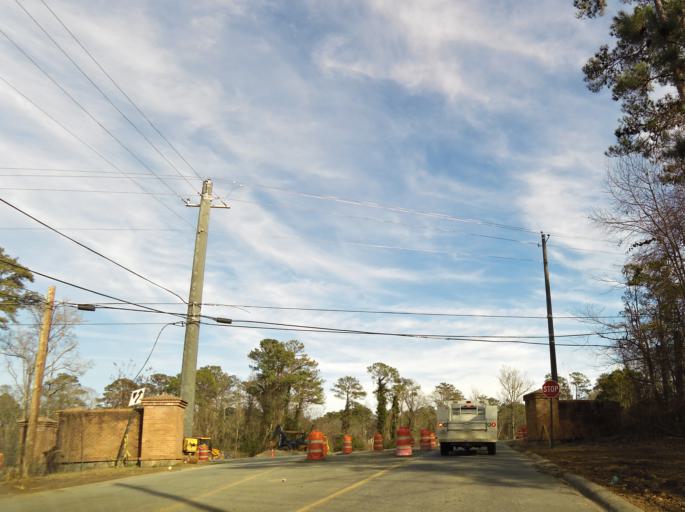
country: US
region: Georgia
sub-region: Bibb County
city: Macon
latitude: 32.8855
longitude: -83.6962
